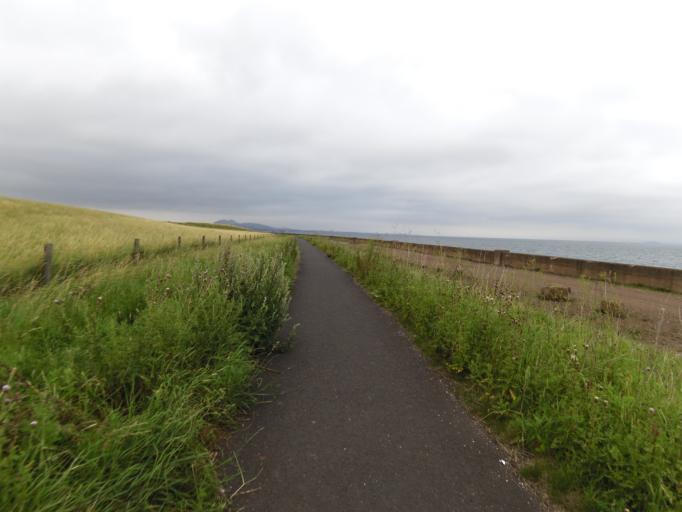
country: GB
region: Scotland
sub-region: East Lothian
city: Musselburgh
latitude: 55.9541
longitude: -3.0363
